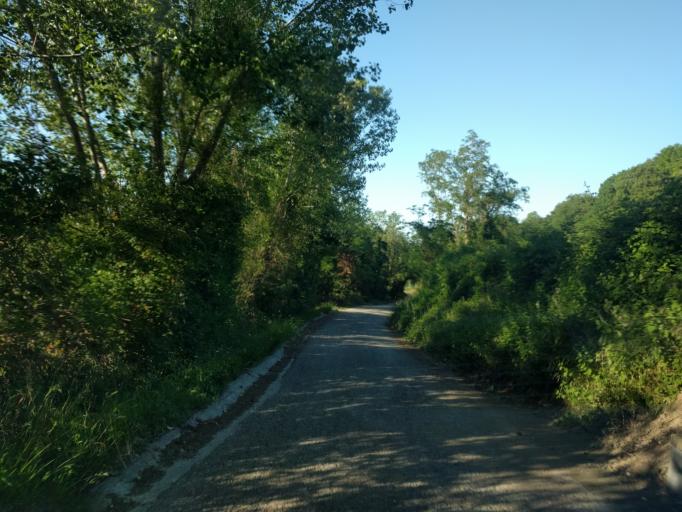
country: IT
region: The Marches
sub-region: Provincia di Pesaro e Urbino
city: Montemaggiore al Metauro
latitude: 43.7388
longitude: 12.9437
